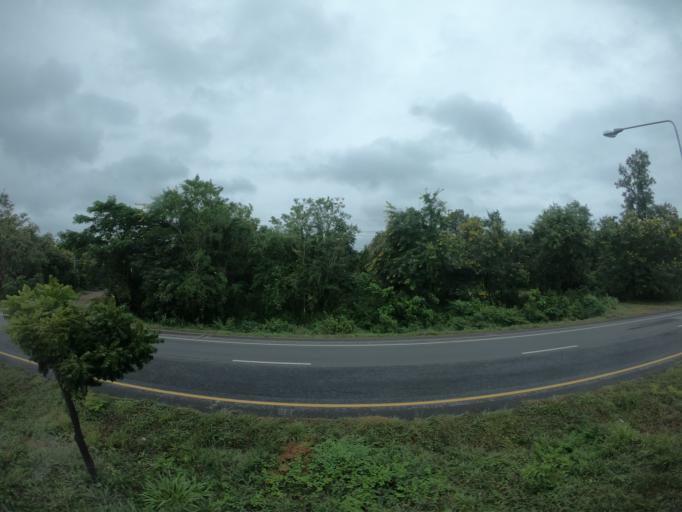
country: TH
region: Nakhon Ratchasima
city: Sida
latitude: 15.5547
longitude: 102.5499
